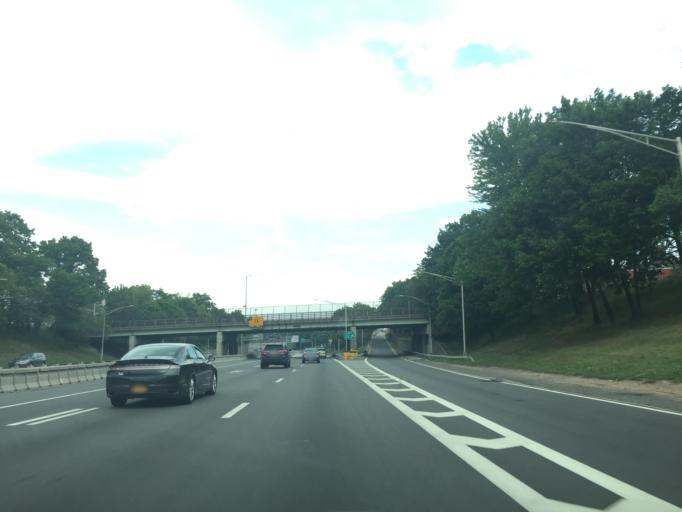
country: US
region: New York
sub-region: Kings County
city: Bensonhurst
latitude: 40.6297
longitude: -74.0171
